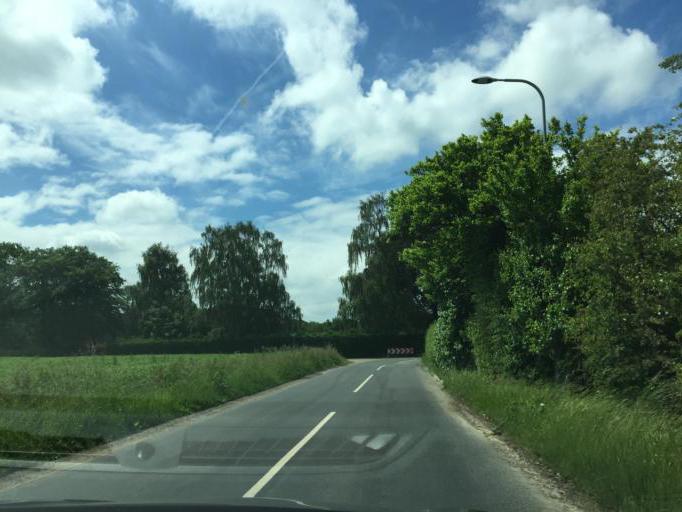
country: DK
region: South Denmark
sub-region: Faaborg-Midtfyn Kommune
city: Ringe
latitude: 55.1989
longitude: 10.4769
